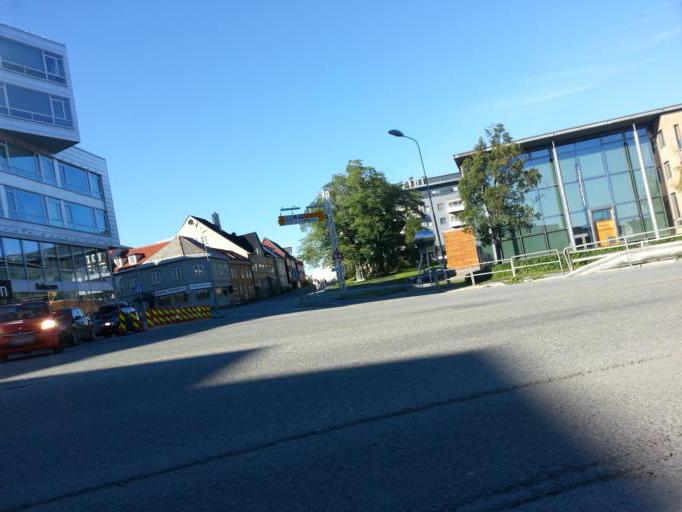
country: NO
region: Troms
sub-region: Tromso
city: Tromso
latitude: 69.6543
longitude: 18.9639
